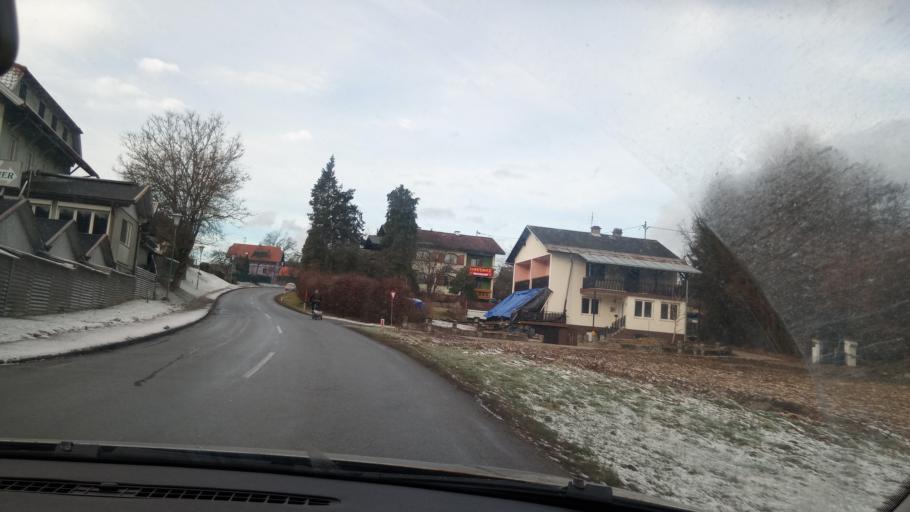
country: AT
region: Carinthia
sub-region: Politischer Bezirk Klagenfurt Land
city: Kottmannsdorf
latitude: 46.5877
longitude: 14.2370
